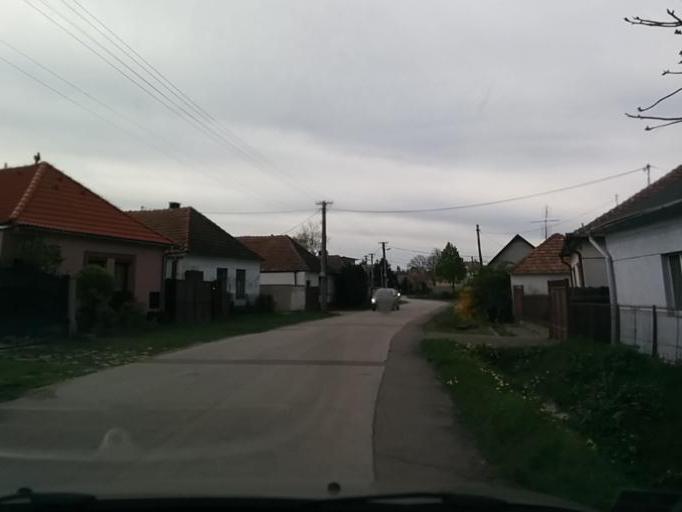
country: SK
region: Trnavsky
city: Sladkovicovo
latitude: 48.2320
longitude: 17.5727
